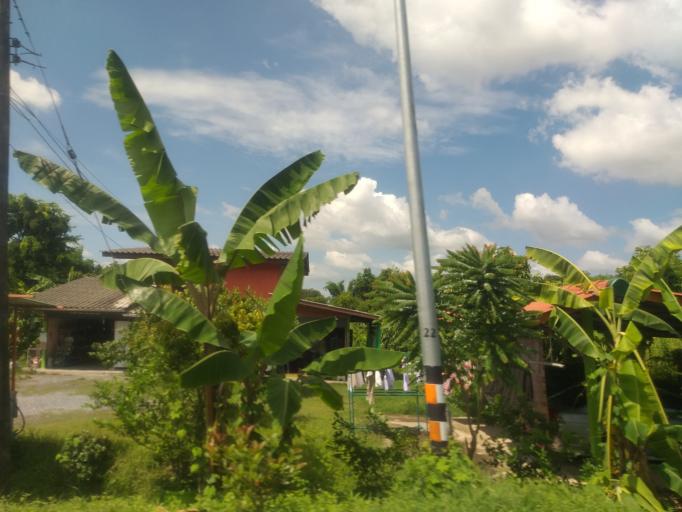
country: TH
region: Nakhon Nayok
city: Nakhon Nayok
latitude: 14.2739
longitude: 101.2891
